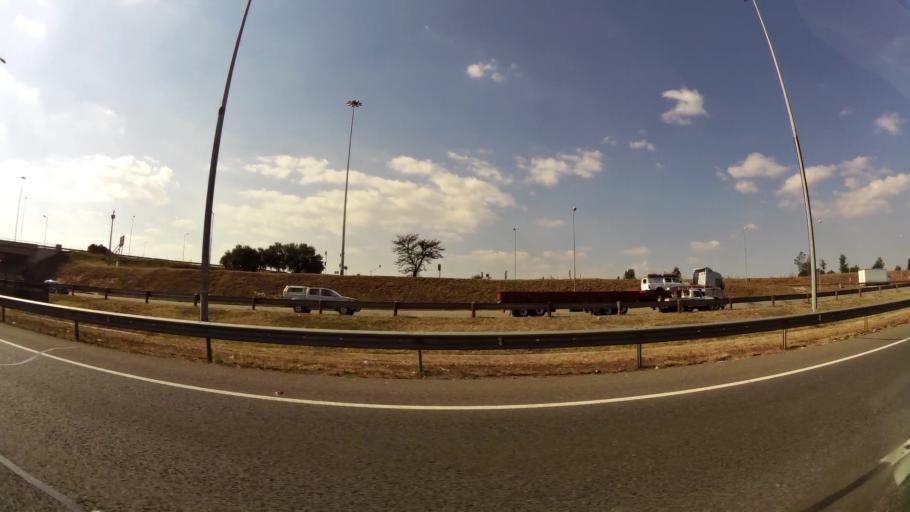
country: ZA
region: Gauteng
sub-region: Ekurhuleni Metropolitan Municipality
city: Tembisa
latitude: -26.0640
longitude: 28.2772
